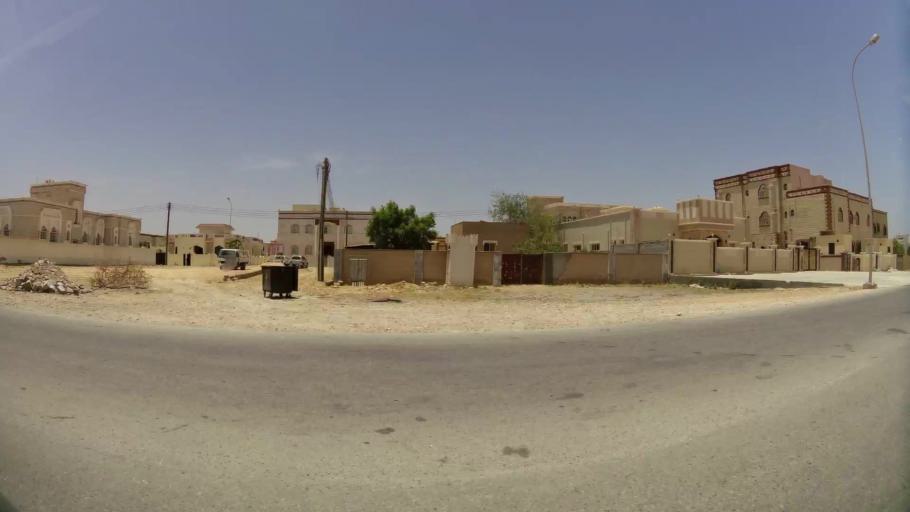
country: OM
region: Zufar
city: Salalah
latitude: 17.0803
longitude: 54.1568
